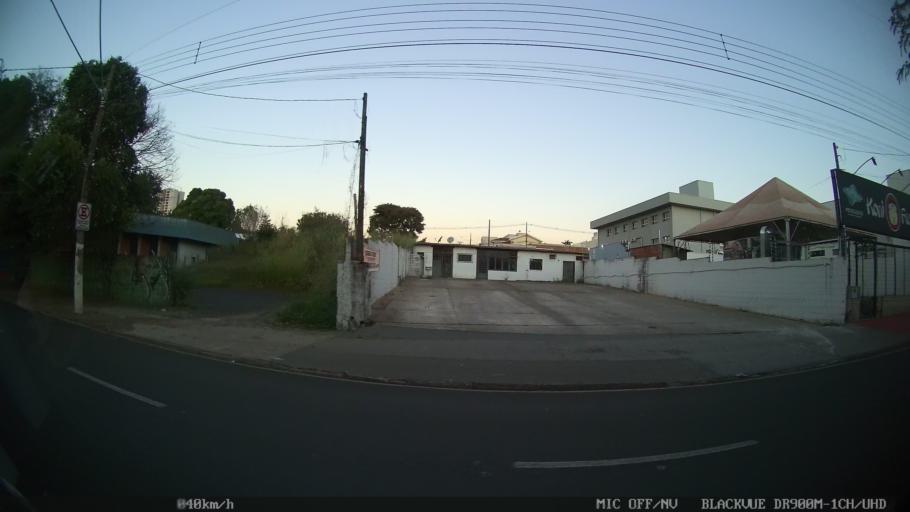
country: BR
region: Sao Paulo
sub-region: Sao Jose Do Rio Preto
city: Sao Jose do Rio Preto
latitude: -20.8289
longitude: -49.3890
